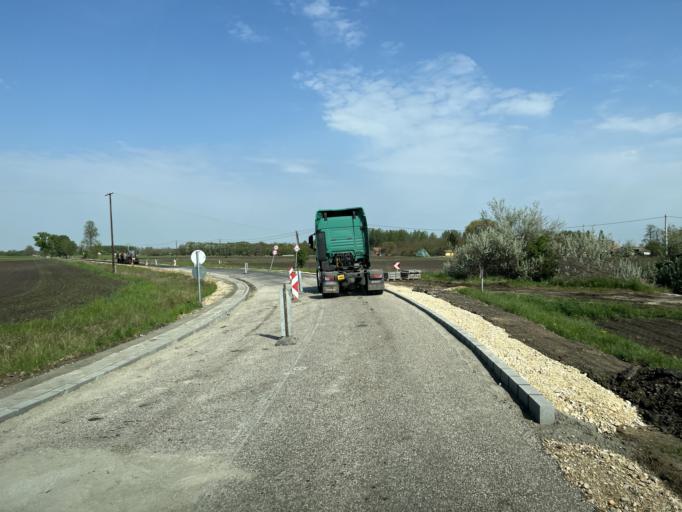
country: HU
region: Pest
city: Kocser
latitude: 46.9860
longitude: 19.9798
